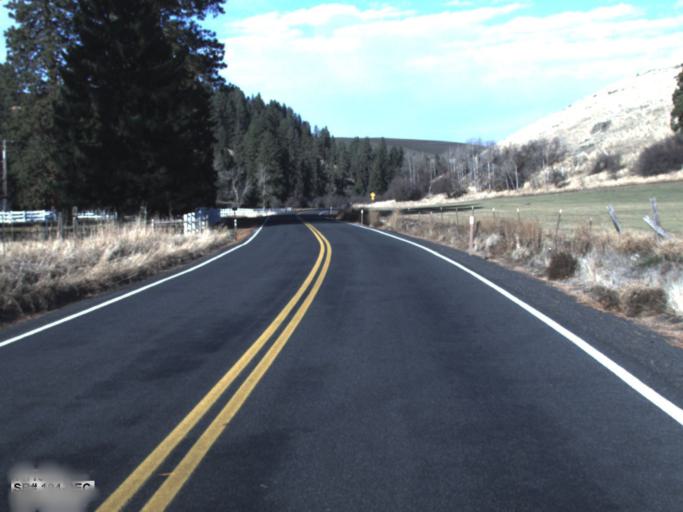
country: US
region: Washington
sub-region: Whitman County
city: Pullman
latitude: 46.7354
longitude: -117.3220
